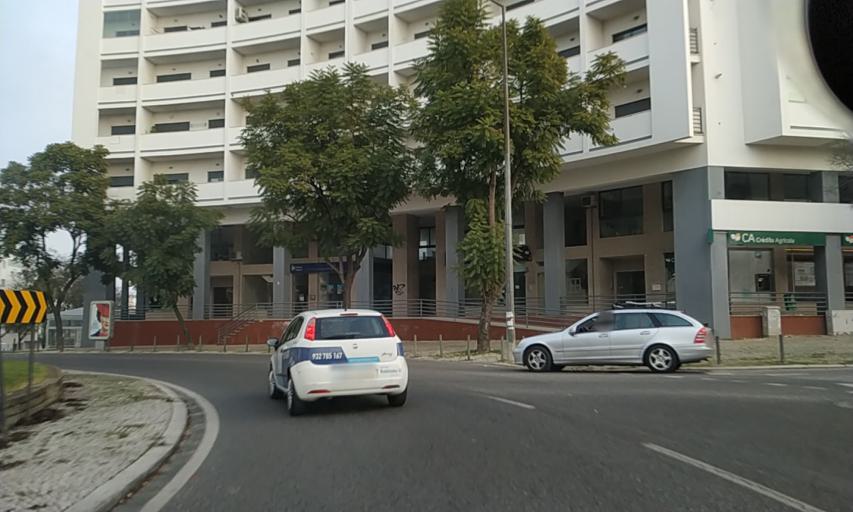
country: PT
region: Setubal
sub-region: Setubal
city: Setubal
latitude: 38.5300
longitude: -8.8750
